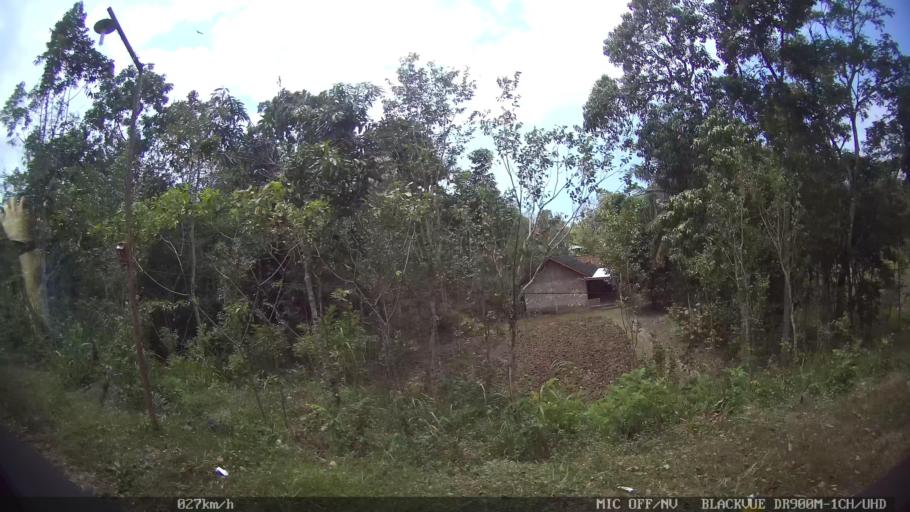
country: ID
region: Central Java
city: Candi Prambanan
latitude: -7.8043
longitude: 110.5211
